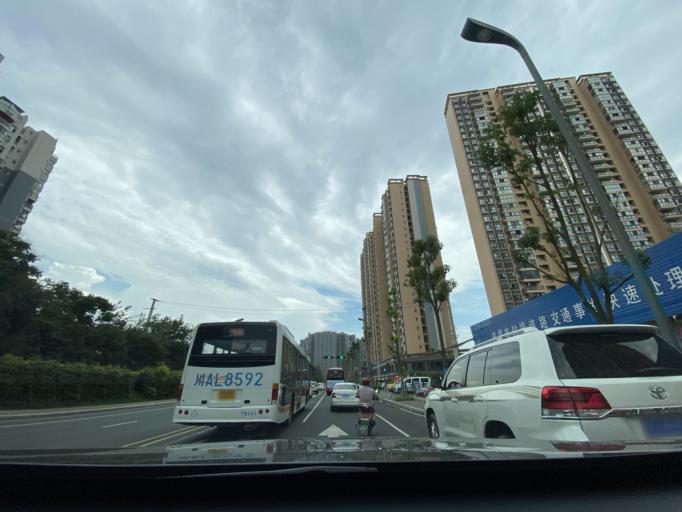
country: CN
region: Sichuan
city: Dongsheng
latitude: 30.5129
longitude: 104.0392
